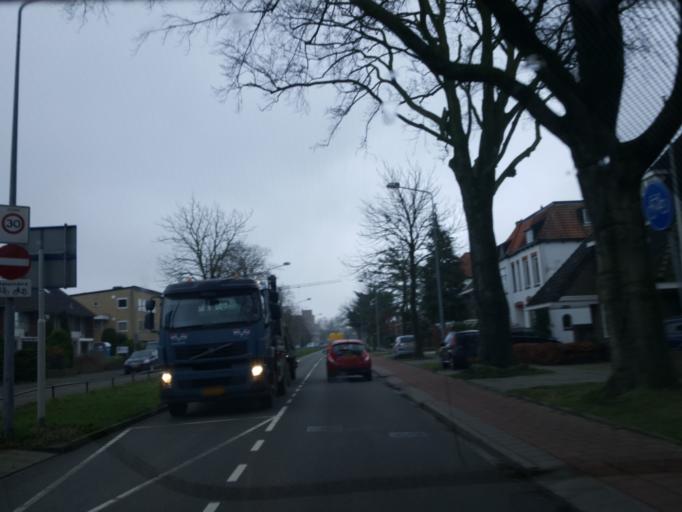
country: NL
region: North Holland
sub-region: Gemeente Hilversum
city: Hilversum
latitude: 52.2183
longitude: 5.1546
